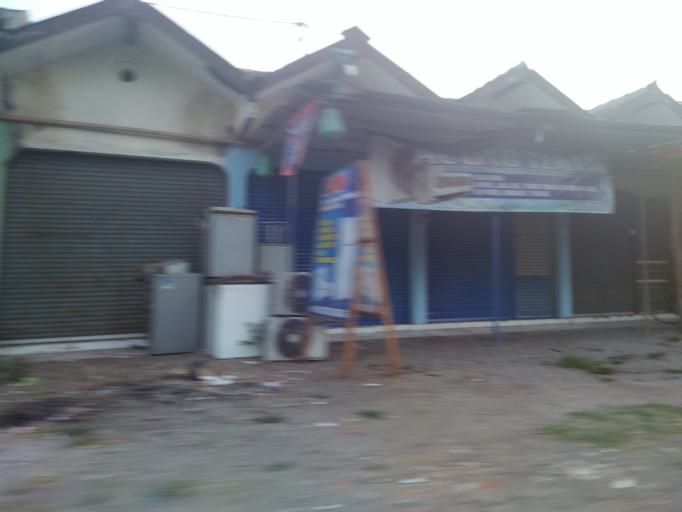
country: ID
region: Daerah Istimewa Yogyakarta
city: Sewon
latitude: -7.8471
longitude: 110.4074
